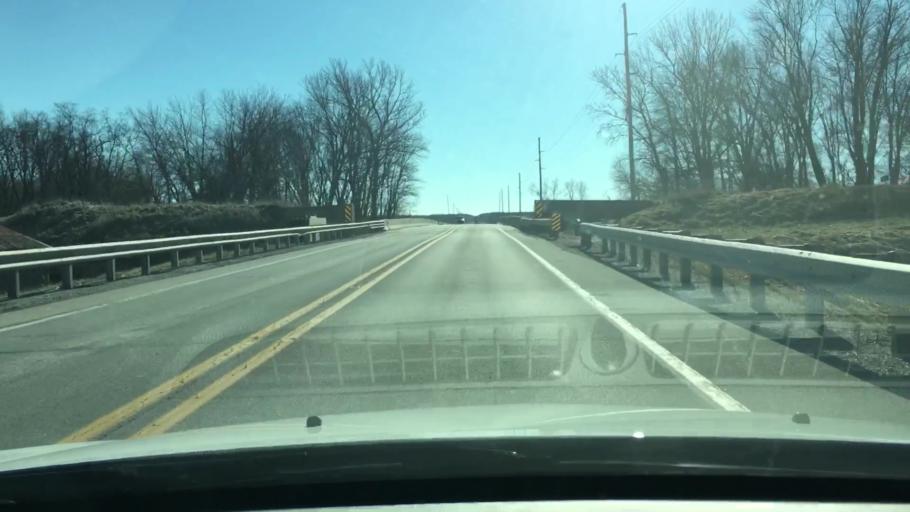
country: US
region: Illinois
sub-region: Cass County
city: Beardstown
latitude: 39.9313
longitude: -90.4947
